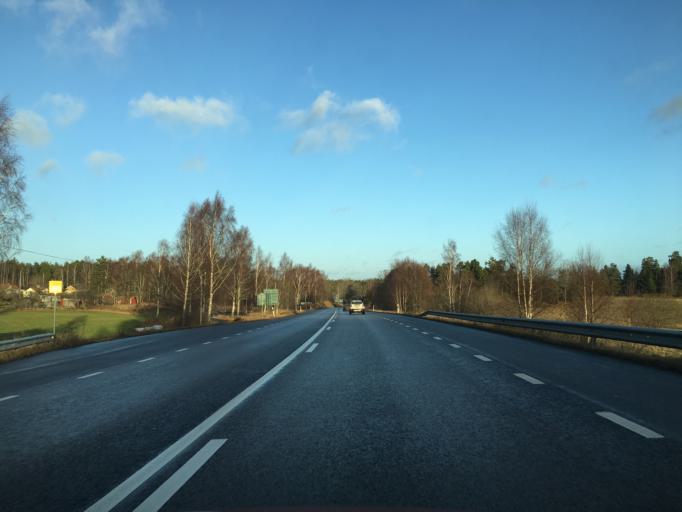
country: SE
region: Kalmar
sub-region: Vasterviks Kommun
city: Ankarsrum
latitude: 57.7145
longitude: 16.4502
